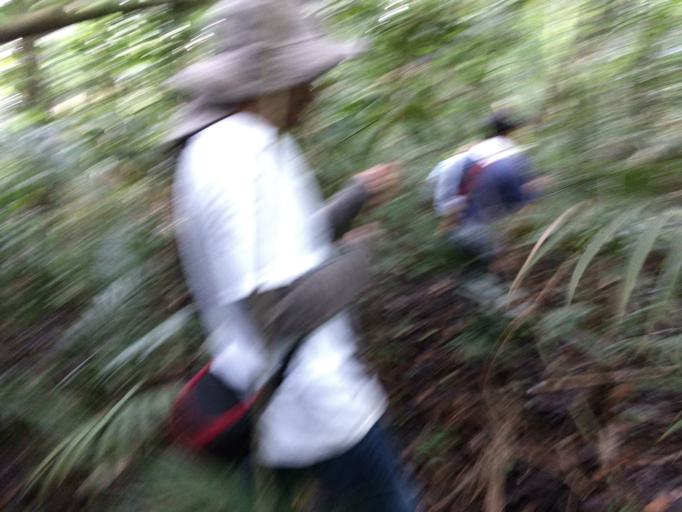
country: CO
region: Antioquia
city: San Rafael
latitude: 6.3152
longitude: -74.8909
